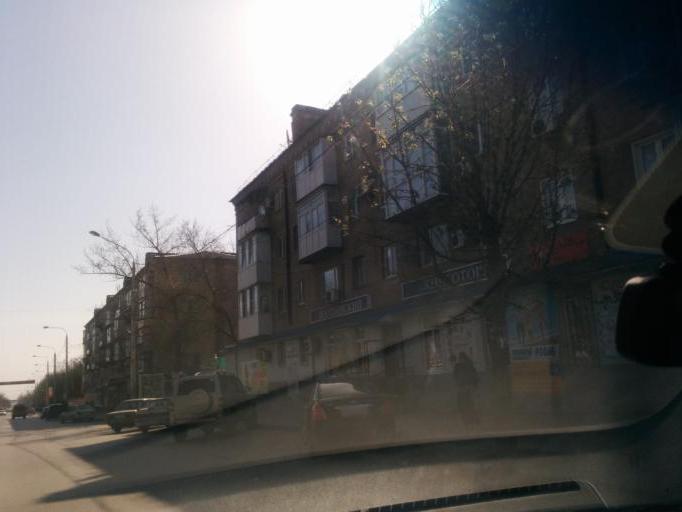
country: RU
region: Rostov
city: Shakhty
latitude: 47.7021
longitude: 40.2107
